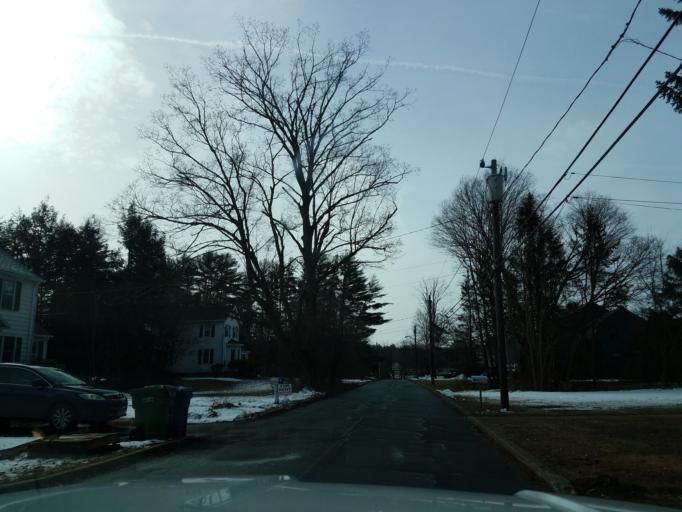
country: US
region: Connecticut
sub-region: Hartford County
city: Weatogue
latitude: 41.8101
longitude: -72.8276
